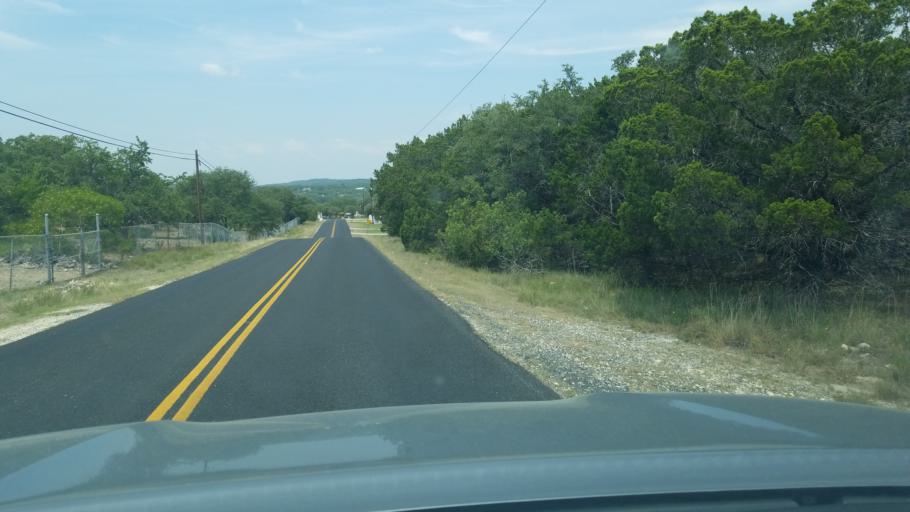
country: US
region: Texas
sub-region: Comal County
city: Bulverde
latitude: 29.7717
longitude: -98.4557
